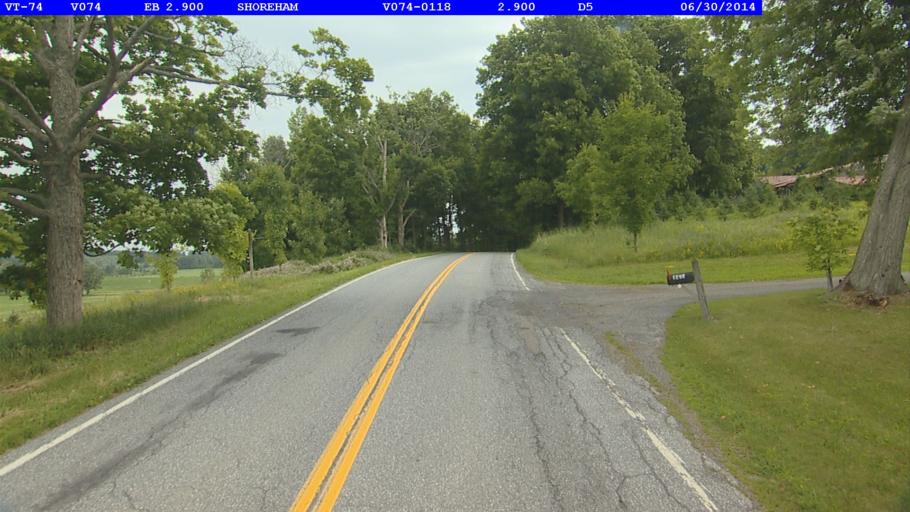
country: US
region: New York
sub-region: Essex County
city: Ticonderoga
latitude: 43.8737
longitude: -73.3340
